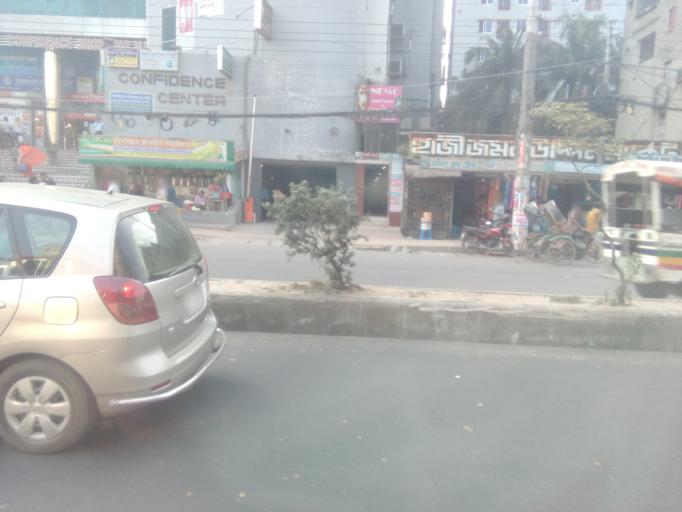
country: BD
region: Dhaka
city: Paltan
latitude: 23.7927
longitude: 90.4241
